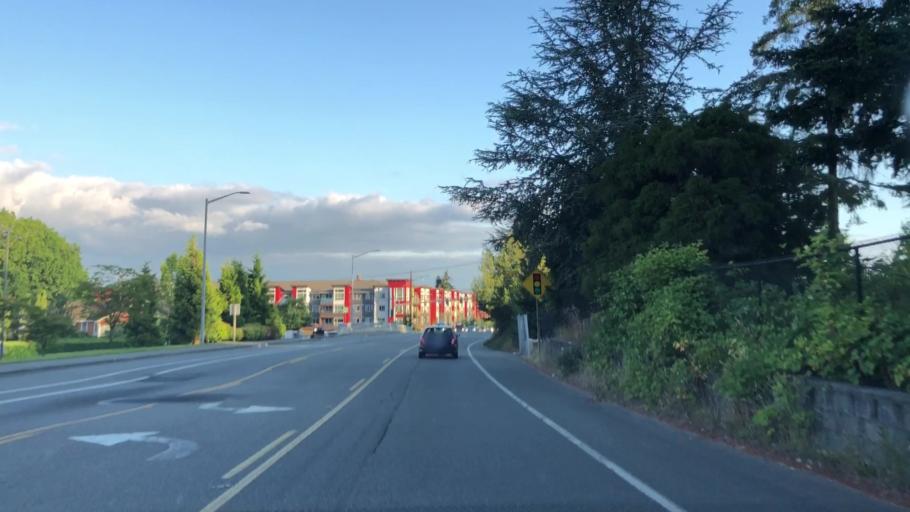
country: US
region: Washington
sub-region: Snohomish County
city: Alderwood Manor
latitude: 47.8516
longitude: -122.2718
